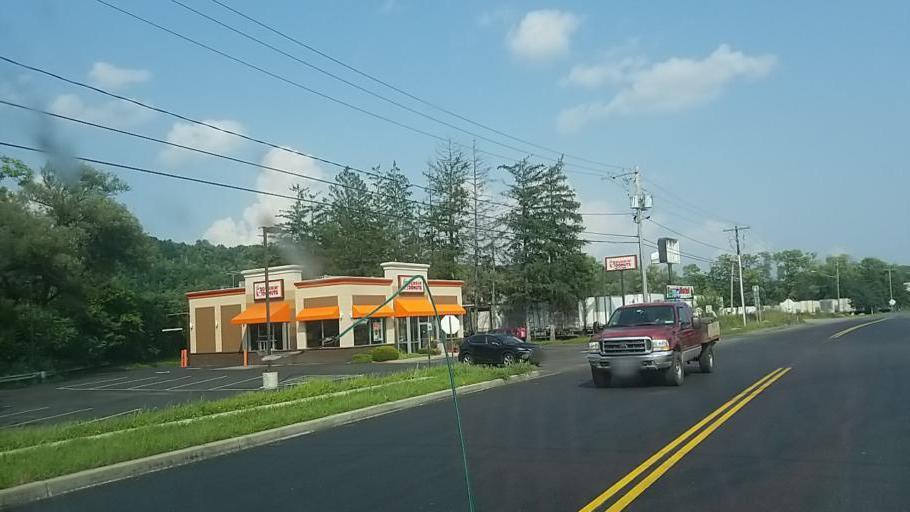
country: US
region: New York
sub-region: Montgomery County
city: Fonda
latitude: 42.9487
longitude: -74.3588
